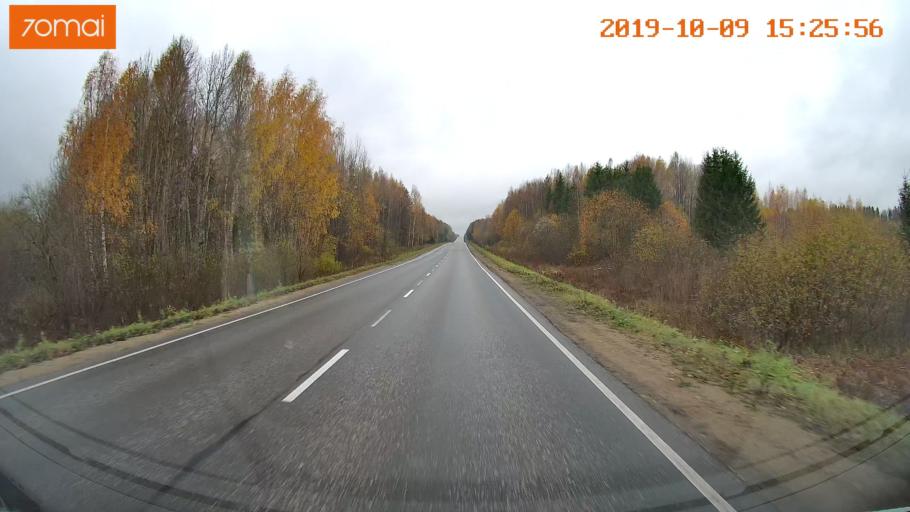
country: RU
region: Kostroma
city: Susanino
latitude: 58.0236
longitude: 41.4165
